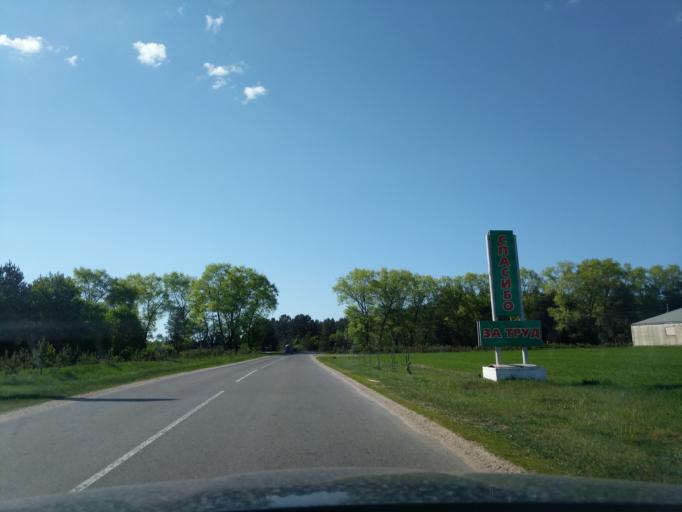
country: BY
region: Vitebsk
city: Pastavy
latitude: 55.1586
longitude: 26.9857
